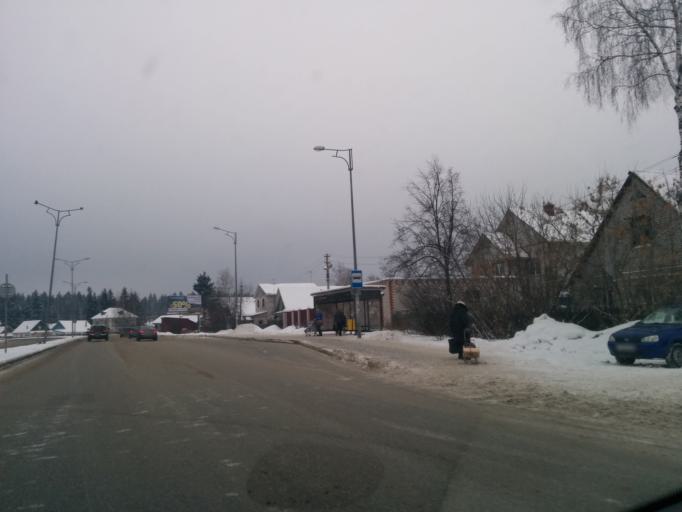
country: RU
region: Perm
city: Kondratovo
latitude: 58.0273
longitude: 56.0004
